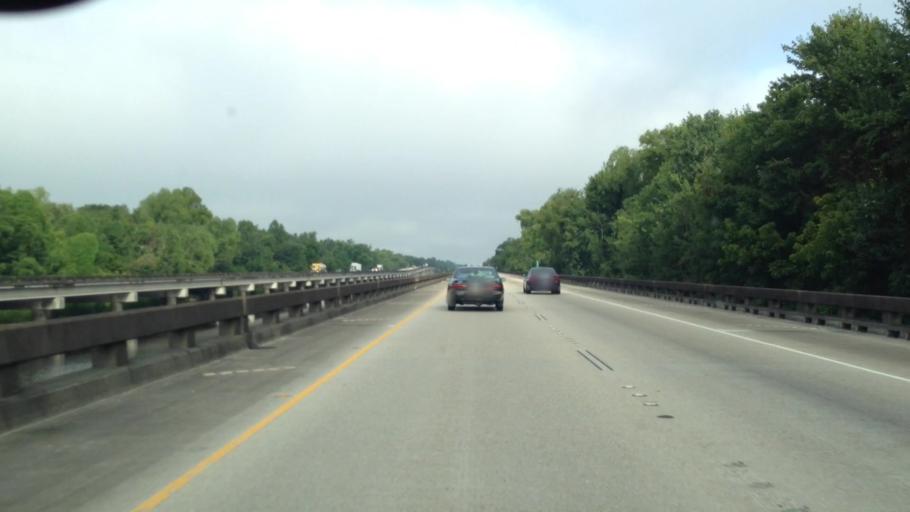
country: US
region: Louisiana
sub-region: Saint John the Baptist Parish
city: Montegut
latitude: 30.1106
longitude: -90.5369
